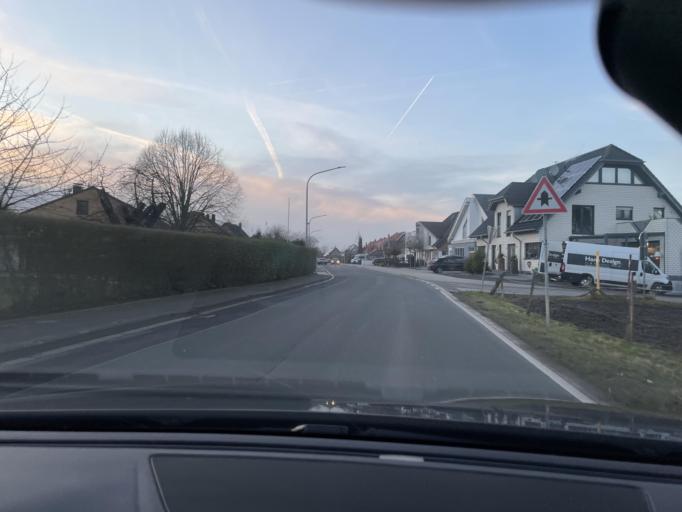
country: DE
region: North Rhine-Westphalia
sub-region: Regierungsbezirk Dusseldorf
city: Viersen
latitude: 51.2339
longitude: 6.4355
